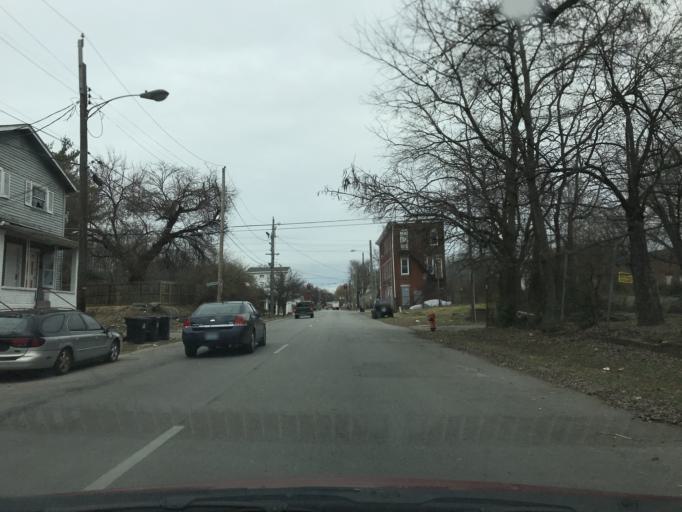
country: US
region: Kentucky
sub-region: Jefferson County
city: Louisville
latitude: 38.2574
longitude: -85.7851
